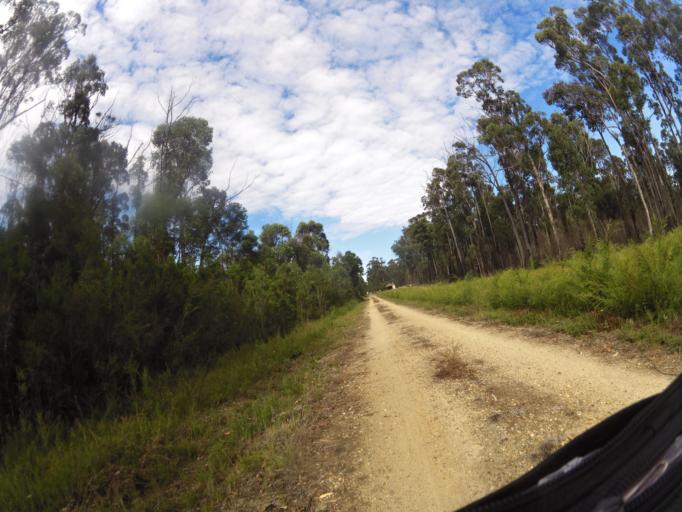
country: AU
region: Victoria
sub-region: East Gippsland
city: Lakes Entrance
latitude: -37.7475
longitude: 148.2272
